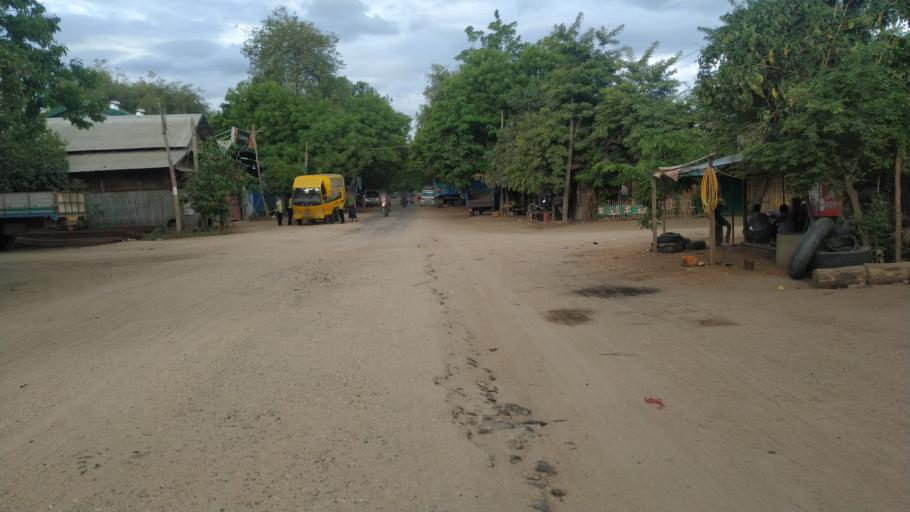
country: MM
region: Magway
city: Pakokku
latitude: 21.3356
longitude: 95.0724
